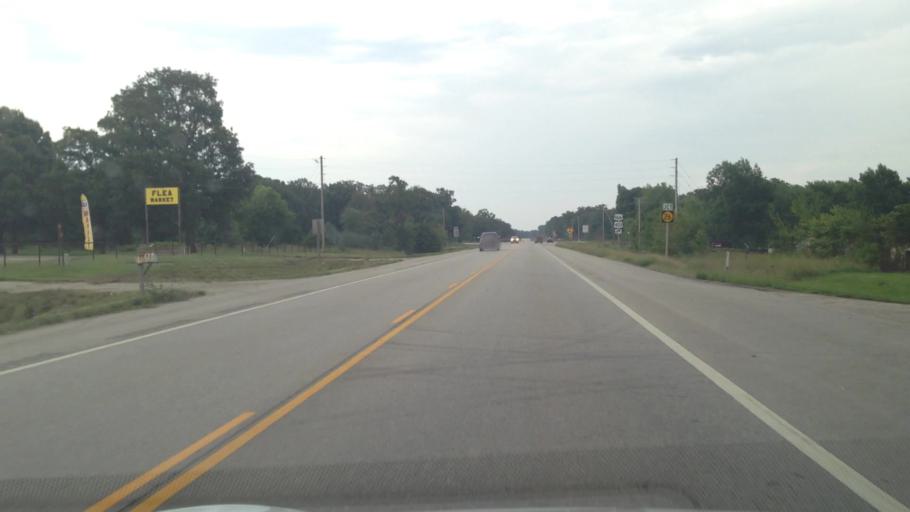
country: US
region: Kansas
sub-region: Cherokee County
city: Galena
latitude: 37.0236
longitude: -94.6470
